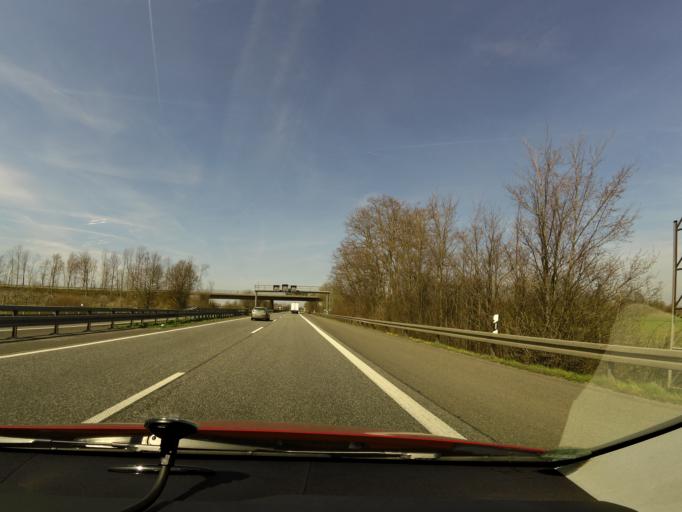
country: DE
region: North Rhine-Westphalia
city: Meckenheim
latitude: 50.5981
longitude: 7.0169
